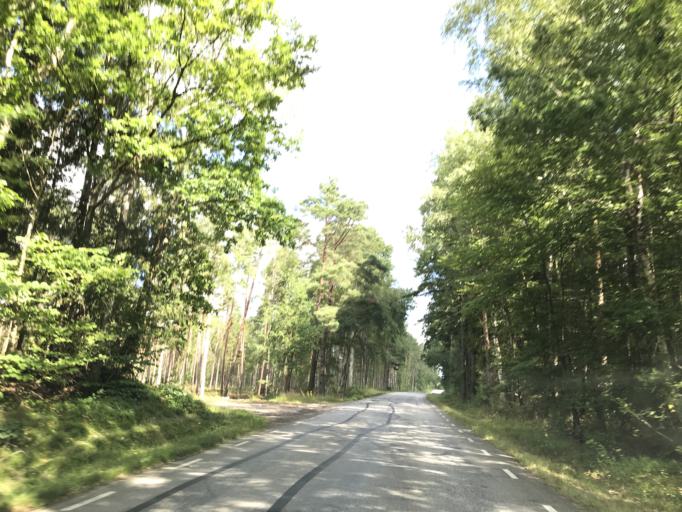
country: SE
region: Halland
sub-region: Laholms Kommun
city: Knared
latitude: 56.4537
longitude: 13.3214
